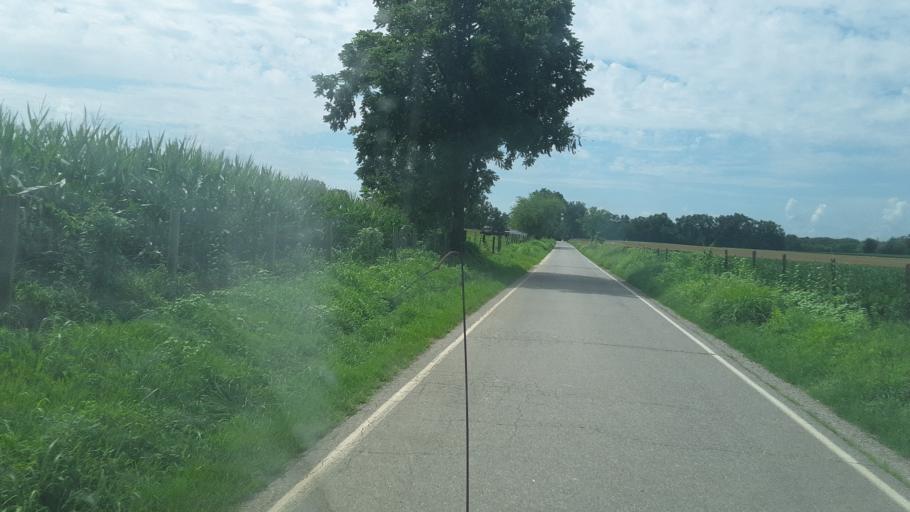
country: US
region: Kentucky
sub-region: Christian County
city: Oak Grove
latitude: 36.6543
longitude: -87.3442
